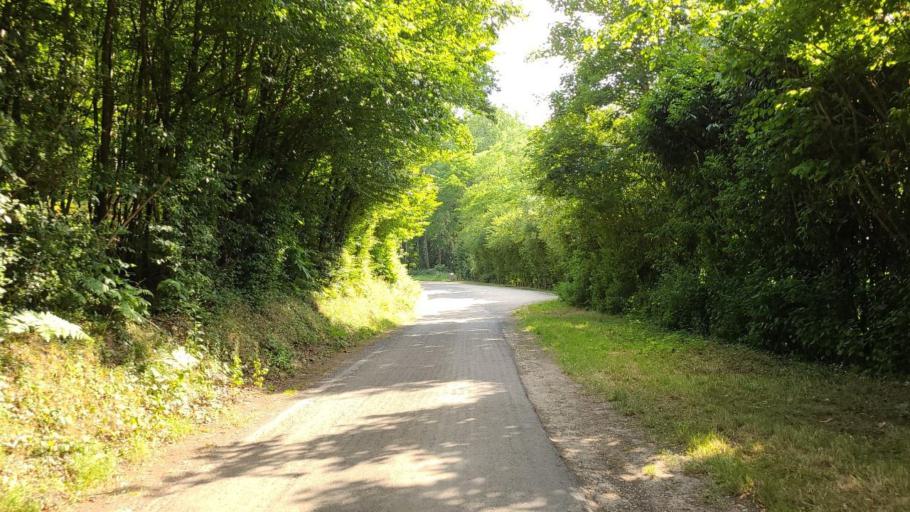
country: FR
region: Centre
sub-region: Departement d'Indre-et-Loire
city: Reugny
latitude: 47.4785
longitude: 0.8902
